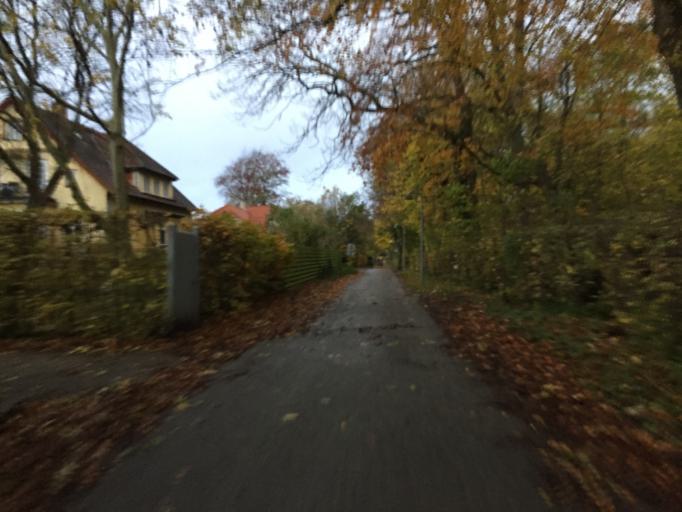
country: DK
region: Zealand
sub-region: Ringsted Kommune
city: Ringsted
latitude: 55.4462
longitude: 11.7960
